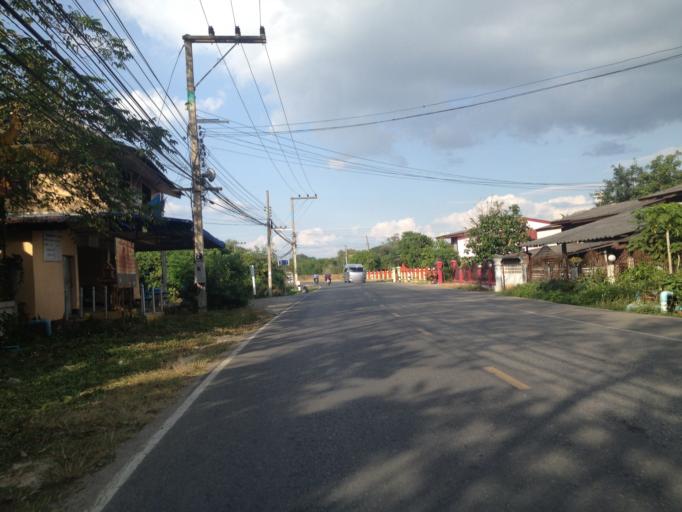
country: TH
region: Chiang Mai
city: Saraphi
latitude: 18.6864
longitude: 98.9853
